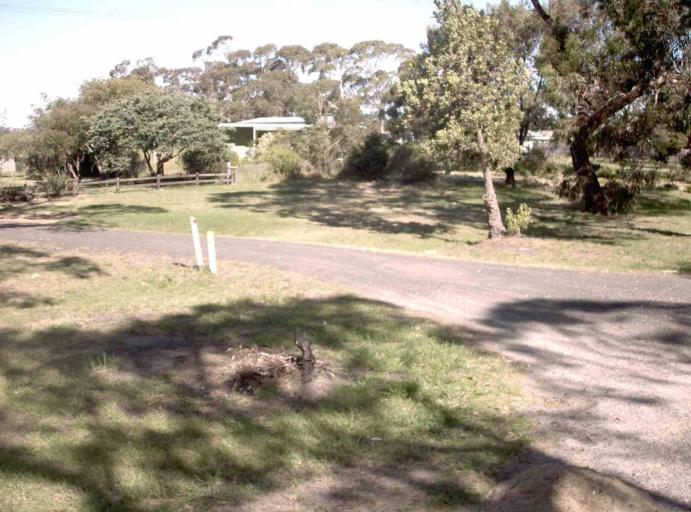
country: AU
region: Victoria
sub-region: Latrobe
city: Traralgon
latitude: -38.6512
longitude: 146.6754
